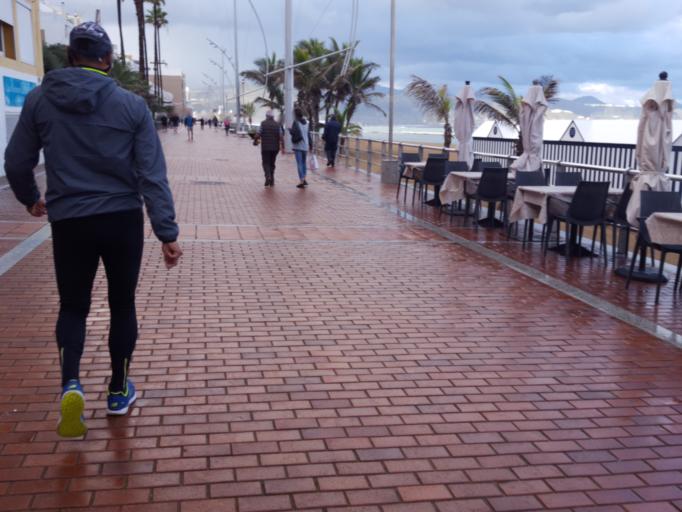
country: ES
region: Canary Islands
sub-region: Provincia de Las Palmas
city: Las Palmas de Gran Canaria
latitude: 28.1431
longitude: -15.4330
